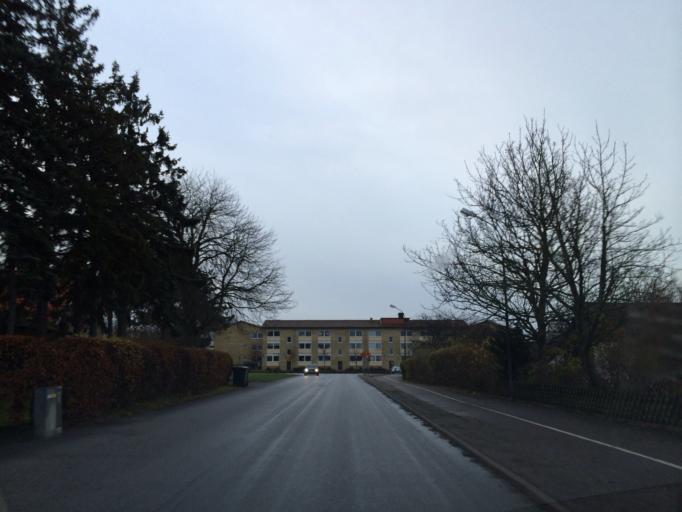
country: SE
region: Skane
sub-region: Lomma Kommun
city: Lomma
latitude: 55.6758
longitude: 13.0862
